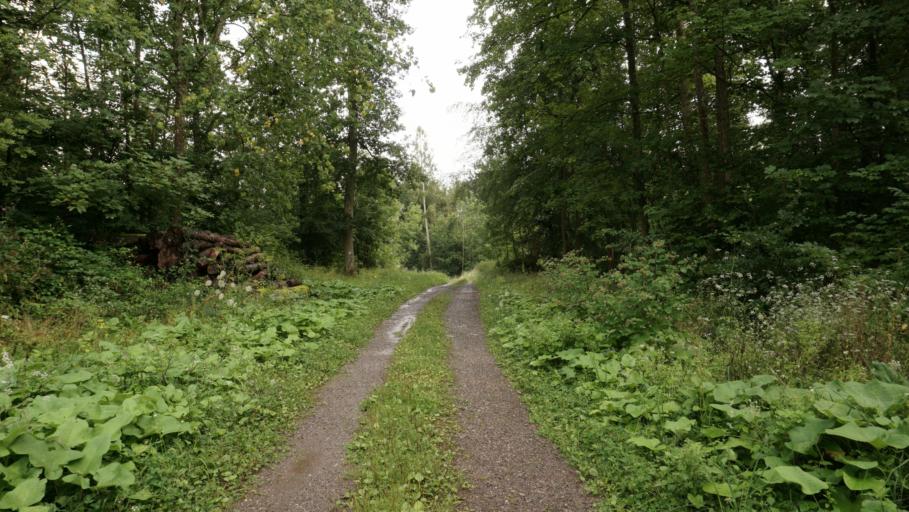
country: DE
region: Baden-Wuerttemberg
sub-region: Karlsruhe Region
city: Hassmersheim
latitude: 49.3177
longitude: 9.1528
